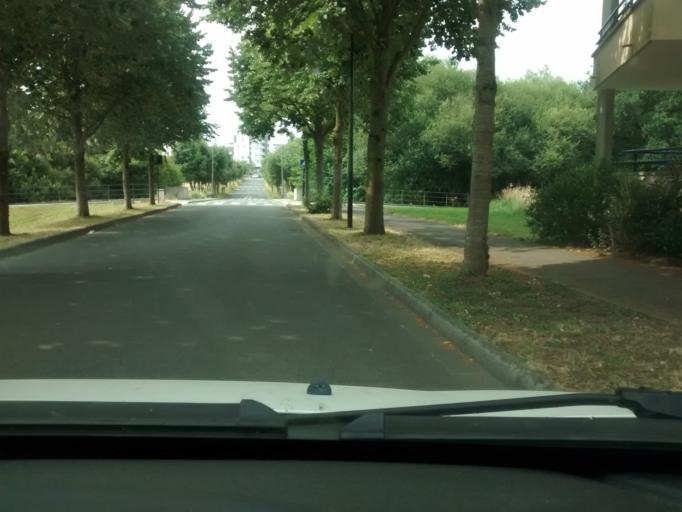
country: FR
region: Brittany
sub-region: Departement d'Ille-et-Vilaine
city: Saint-Jacques-de-la-Lande
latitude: 48.0849
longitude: -1.7121
